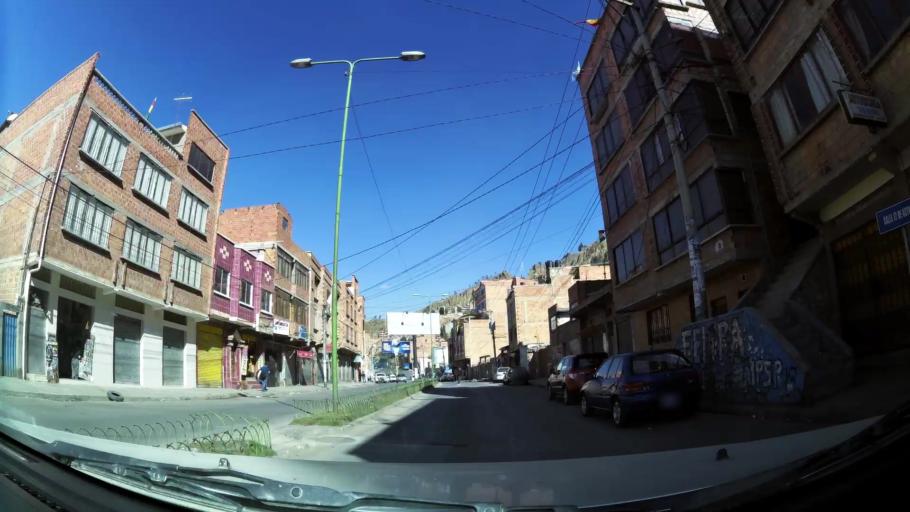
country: BO
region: La Paz
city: La Paz
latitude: -16.5144
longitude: -68.1440
